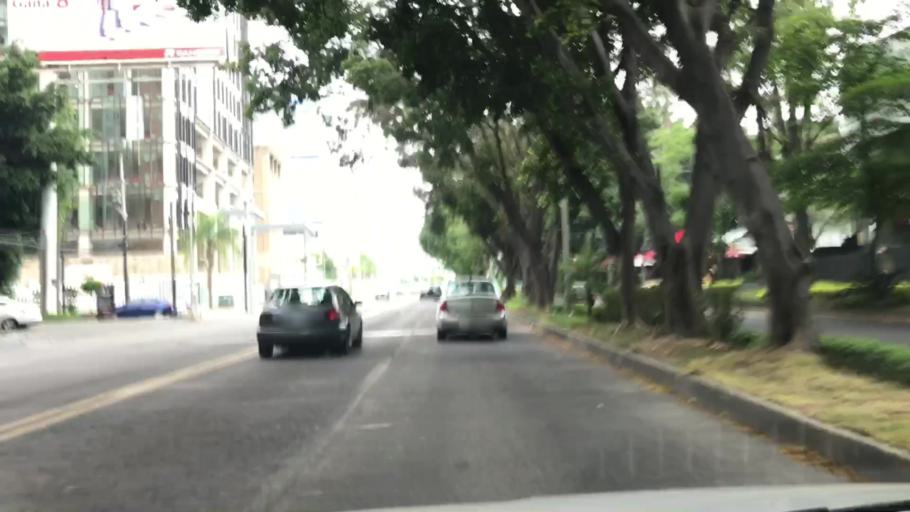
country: MX
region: Jalisco
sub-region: Zapopan
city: Zapopan
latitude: 20.7023
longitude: -103.3759
